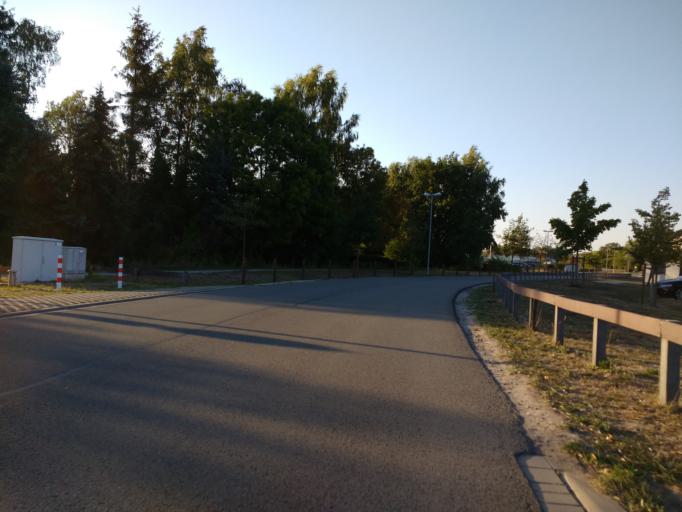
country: DE
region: Lower Saxony
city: Gifhorn
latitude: 52.4957
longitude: 10.5467
